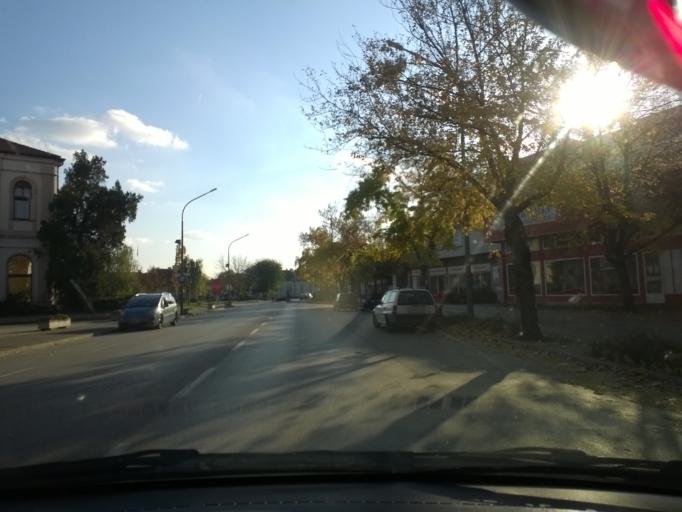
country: HU
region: Csongrad
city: Szentes
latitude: 46.6530
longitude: 20.2665
